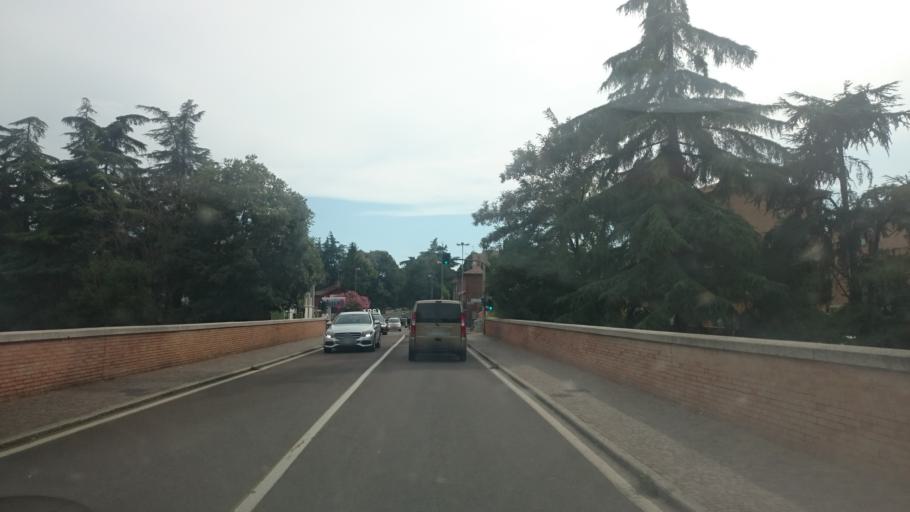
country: IT
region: Emilia-Romagna
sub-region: Provincia di Reggio Emilia
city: Reggio nell'Emilia
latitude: 44.6839
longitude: 10.6229
